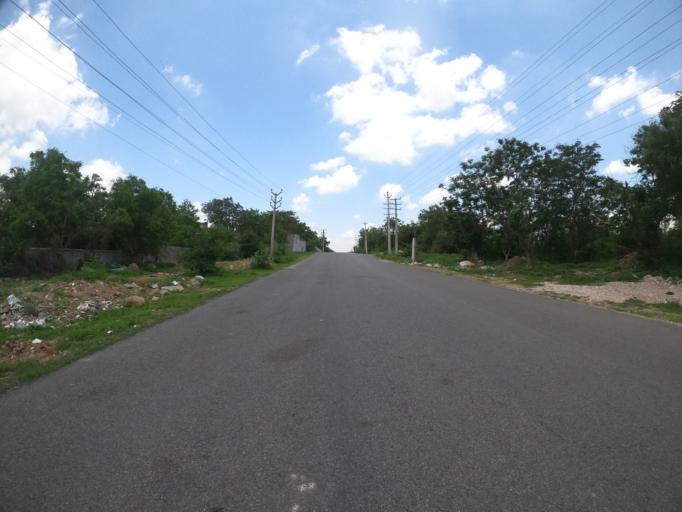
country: IN
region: Telangana
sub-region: Medak
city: Serilingampalle
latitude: 17.3919
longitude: 78.3139
